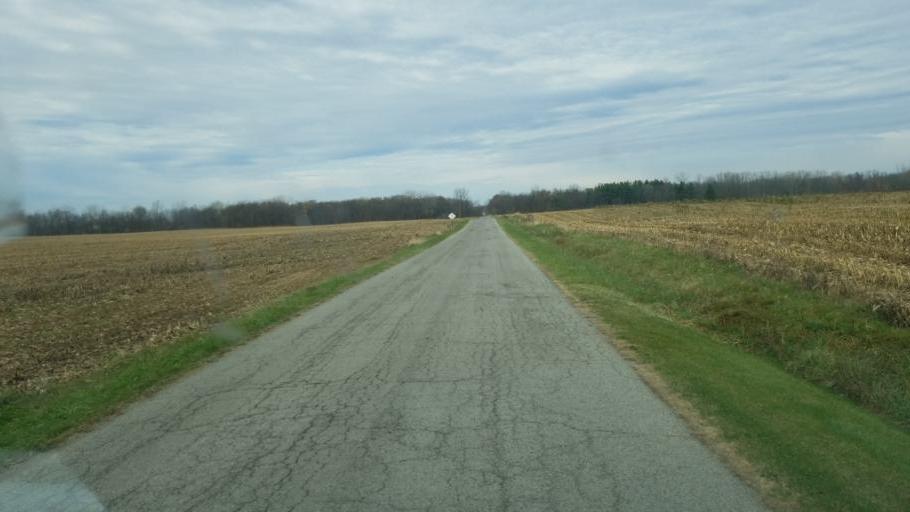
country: US
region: Ohio
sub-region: Knox County
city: Fredericktown
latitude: 40.4894
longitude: -82.6869
